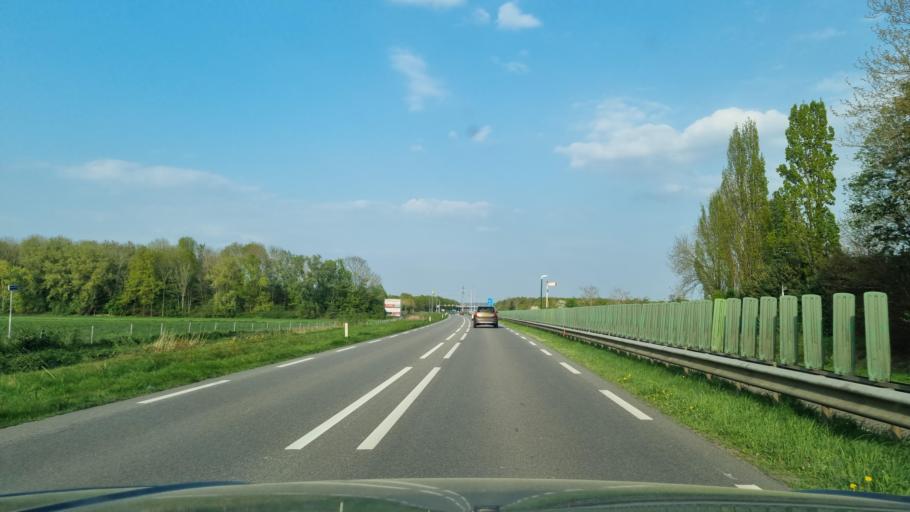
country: NL
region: North Brabant
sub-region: Gemeente Cuijk
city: Cuijk
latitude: 51.7281
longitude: 5.8399
